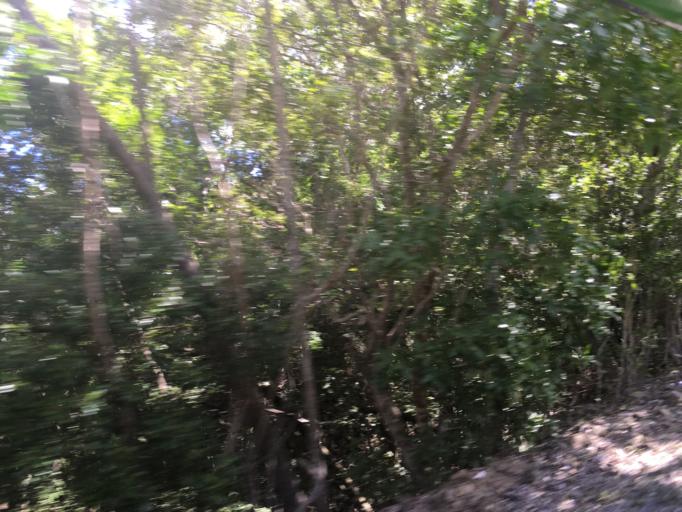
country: VI
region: Saint John Island
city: Cruz Bay
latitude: 18.3508
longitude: -64.7718
